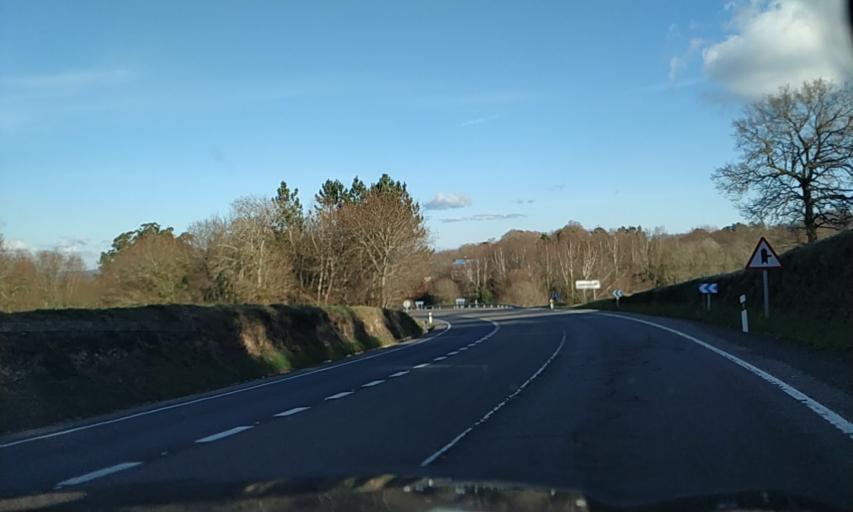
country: ES
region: Galicia
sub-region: Provincia de Pontevedra
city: Silleda
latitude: 42.6973
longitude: -8.3264
